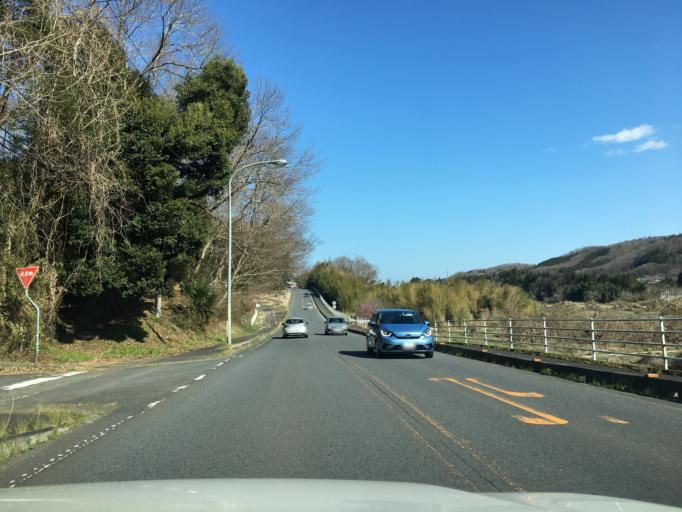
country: JP
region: Tochigi
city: Motegi
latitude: 36.5618
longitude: 140.2611
